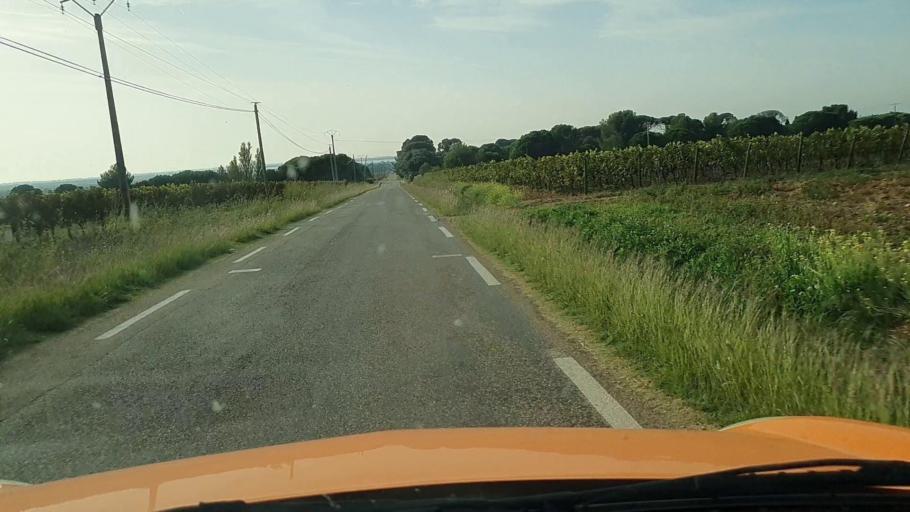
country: FR
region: Languedoc-Roussillon
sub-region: Departement du Gard
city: Beauvoisin
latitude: 43.6617
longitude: 4.3433
